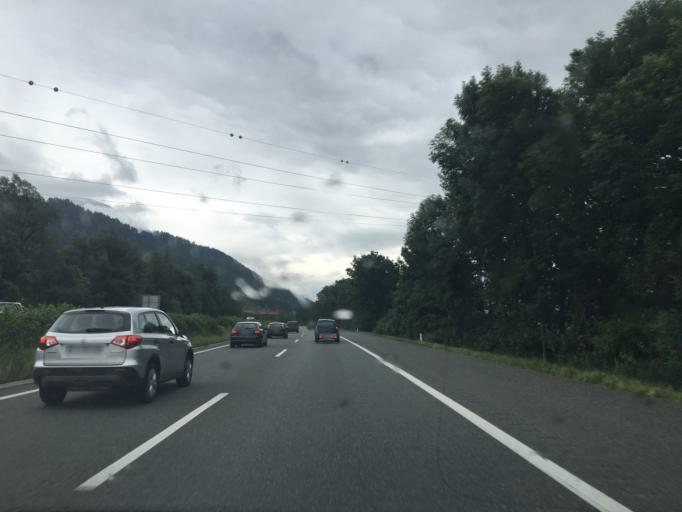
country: AT
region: Tyrol
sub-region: Politischer Bezirk Innsbruck Land
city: Wattenberg
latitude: 47.3015
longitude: 11.6074
